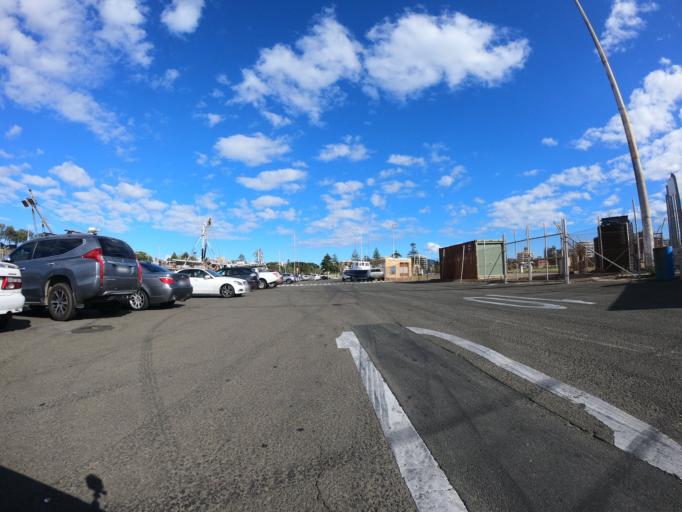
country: AU
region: New South Wales
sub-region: Wollongong
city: Wollongong
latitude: -34.4205
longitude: 150.9075
